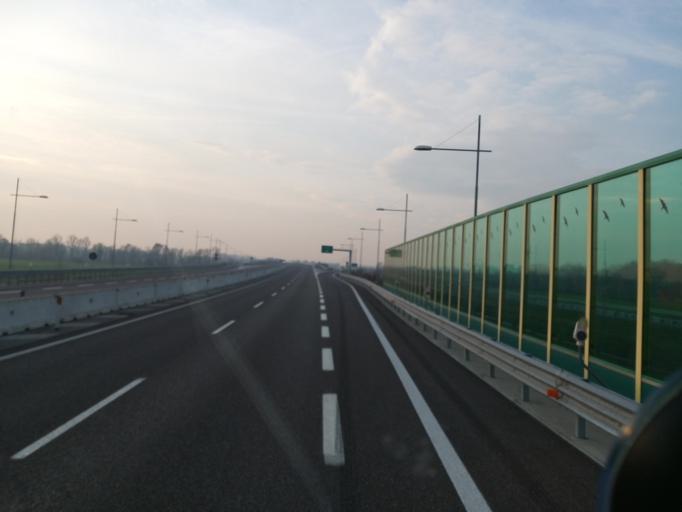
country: IT
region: Lombardy
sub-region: Provincia di Brescia
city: Flero
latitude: 45.4769
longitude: 10.1647
